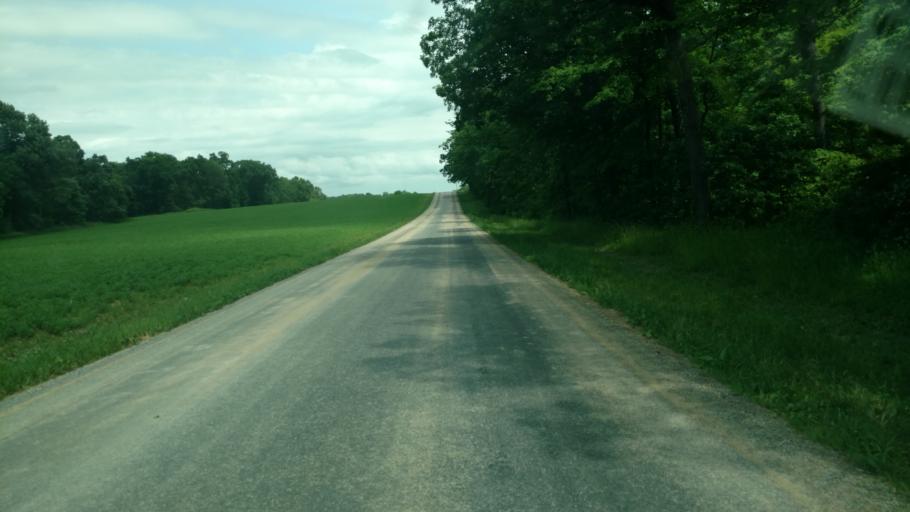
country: US
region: Wisconsin
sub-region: Monroe County
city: Cashton
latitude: 43.6924
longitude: -90.6574
